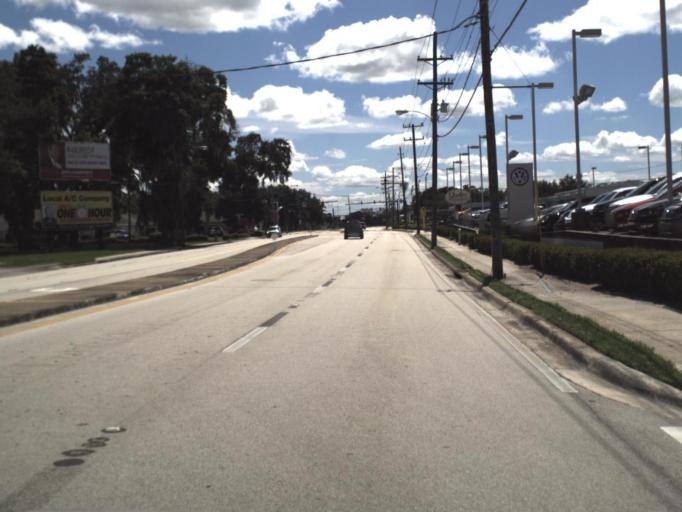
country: US
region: Florida
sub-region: Polk County
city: Lakeland
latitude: 28.0430
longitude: -81.9409
